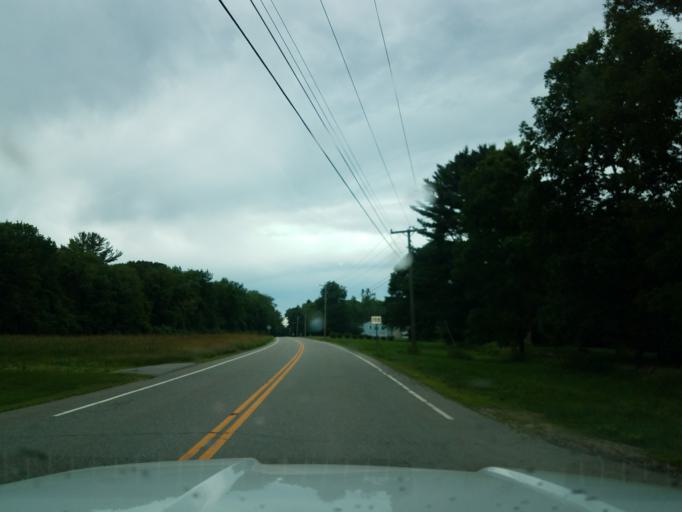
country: US
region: Massachusetts
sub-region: Worcester County
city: Southbridge
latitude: 41.9687
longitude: -72.0815
